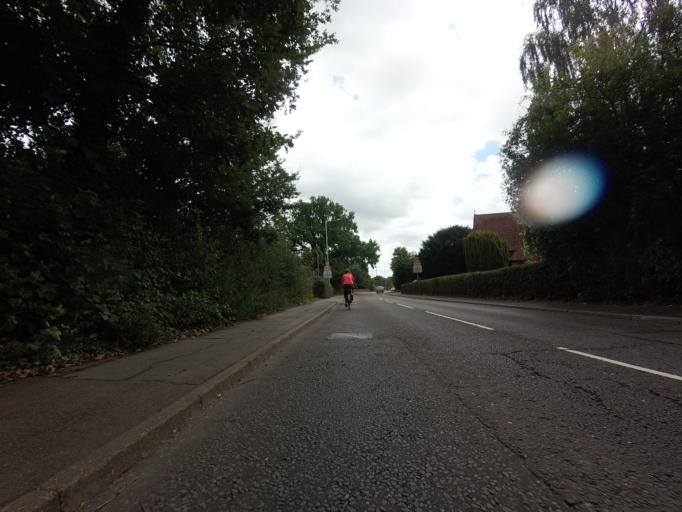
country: GB
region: England
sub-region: Kent
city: Shoreham
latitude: 51.2991
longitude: 0.1627
